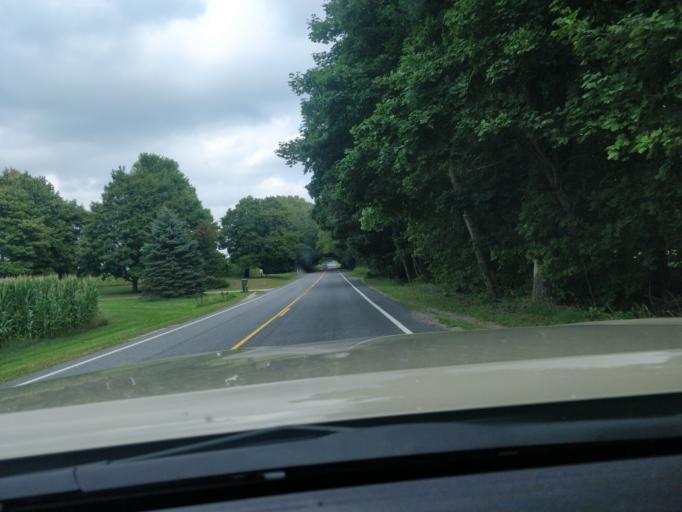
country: US
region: Michigan
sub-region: Kent County
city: Lowell
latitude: 42.8860
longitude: -85.2885
